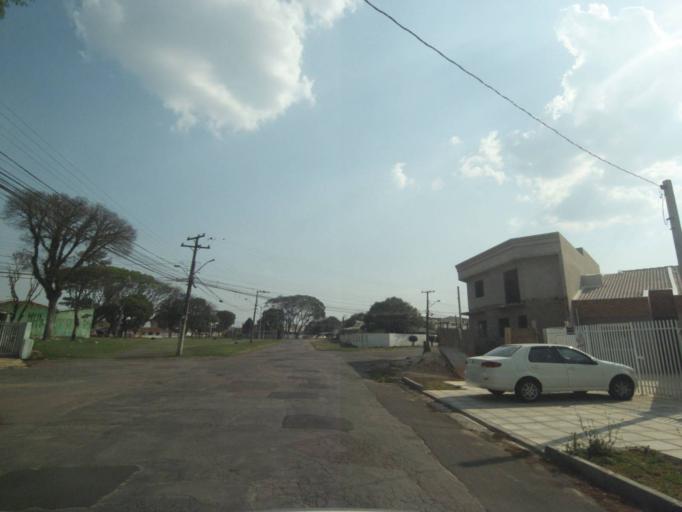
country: BR
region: Parana
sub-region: Sao Jose Dos Pinhais
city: Sao Jose dos Pinhais
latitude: -25.5356
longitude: -49.2371
